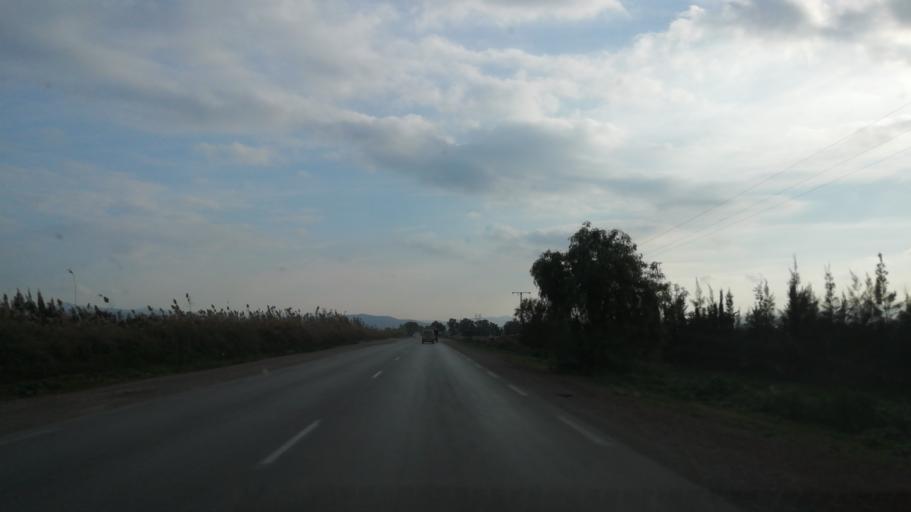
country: DZ
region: Mascara
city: Mascara
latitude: 35.6438
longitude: 0.0601
